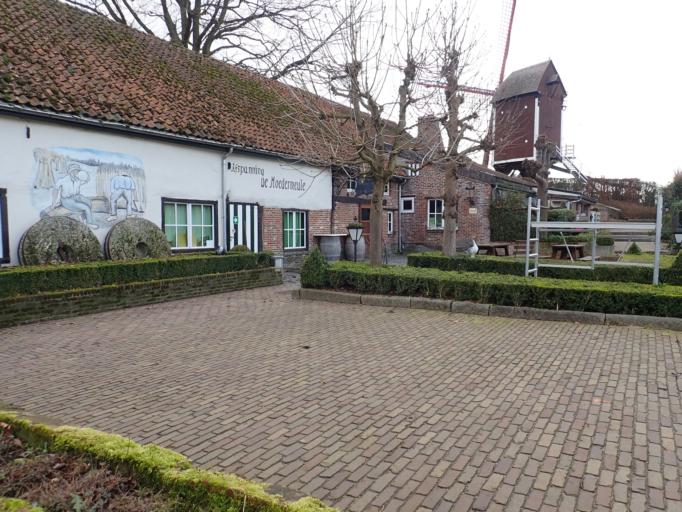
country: BE
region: Flanders
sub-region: Provincie Vlaams-Brabant
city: Aarschot
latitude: 50.9615
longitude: 4.7944
